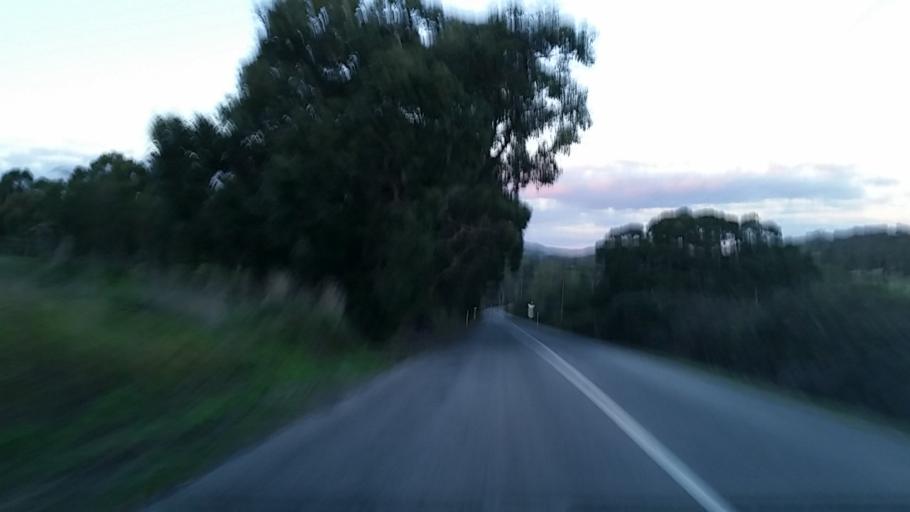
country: AU
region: South Australia
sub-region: Alexandrina
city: Mount Compass
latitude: -35.3171
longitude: 138.6347
